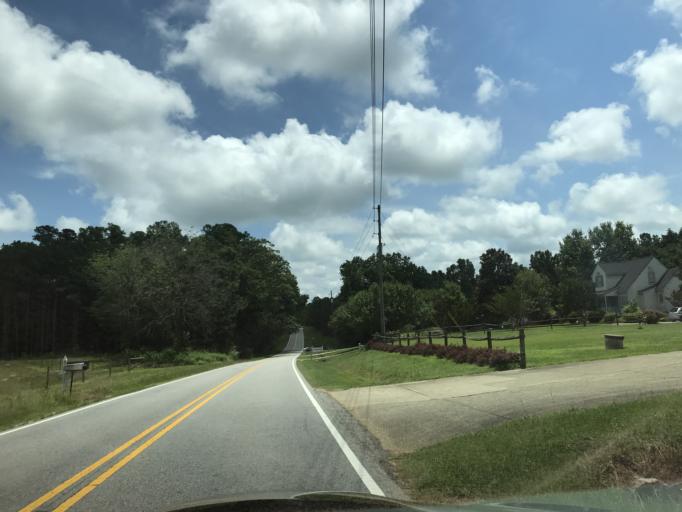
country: US
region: North Carolina
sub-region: Wake County
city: Rolesville
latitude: 35.9546
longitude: -78.3911
